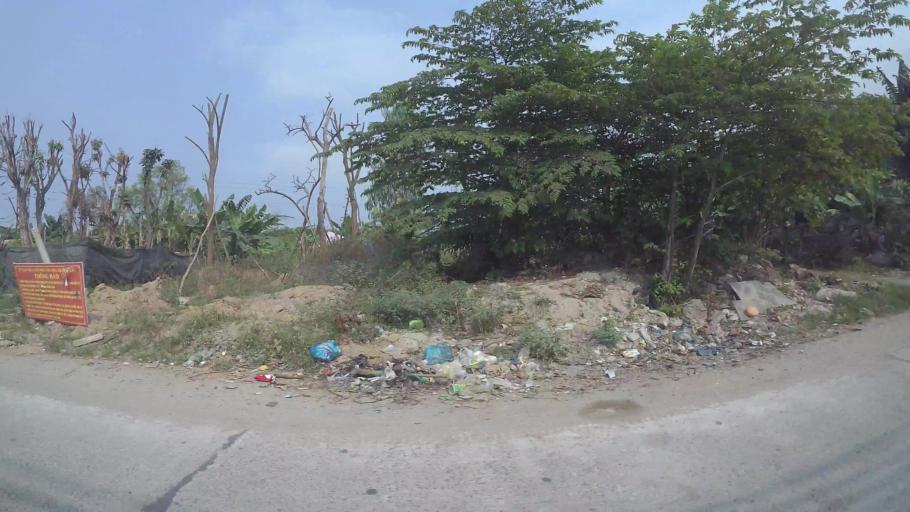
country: VN
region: Da Nang
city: Lien Chieu
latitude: 16.0578
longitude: 108.1567
